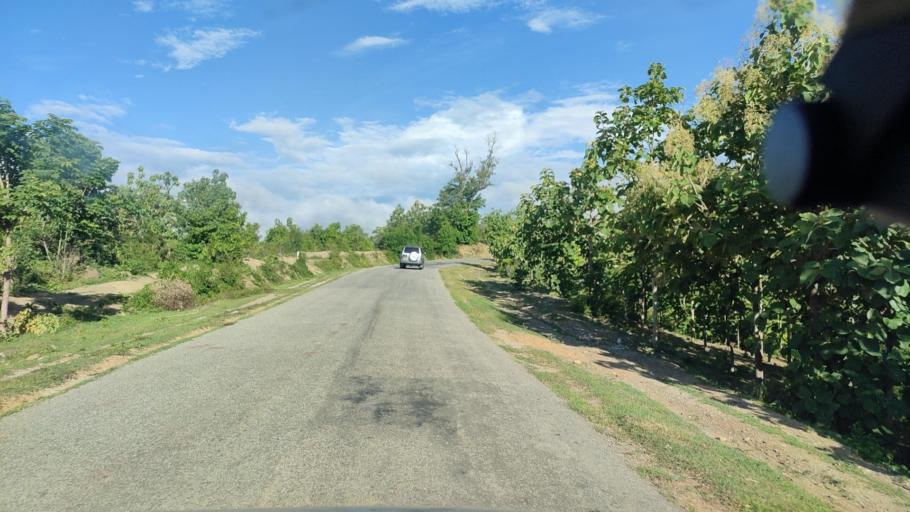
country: MM
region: Magway
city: Taungdwingyi
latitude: 20.0748
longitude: 95.7617
